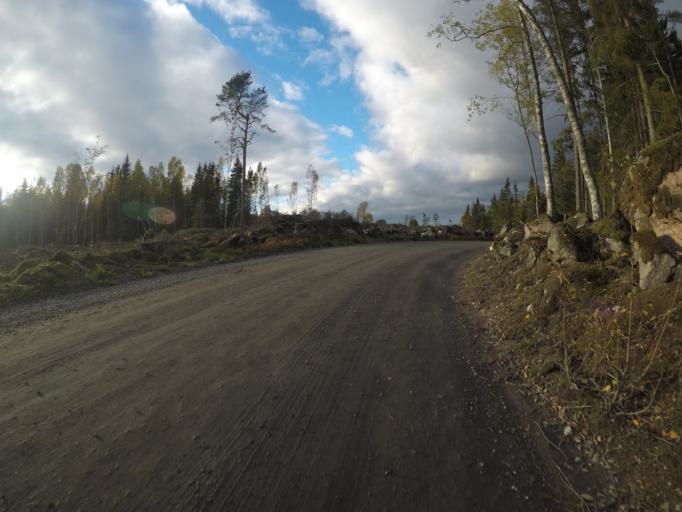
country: SE
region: Vaestmanland
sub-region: Arboga Kommun
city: Tyringe
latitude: 59.2981
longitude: 15.9807
